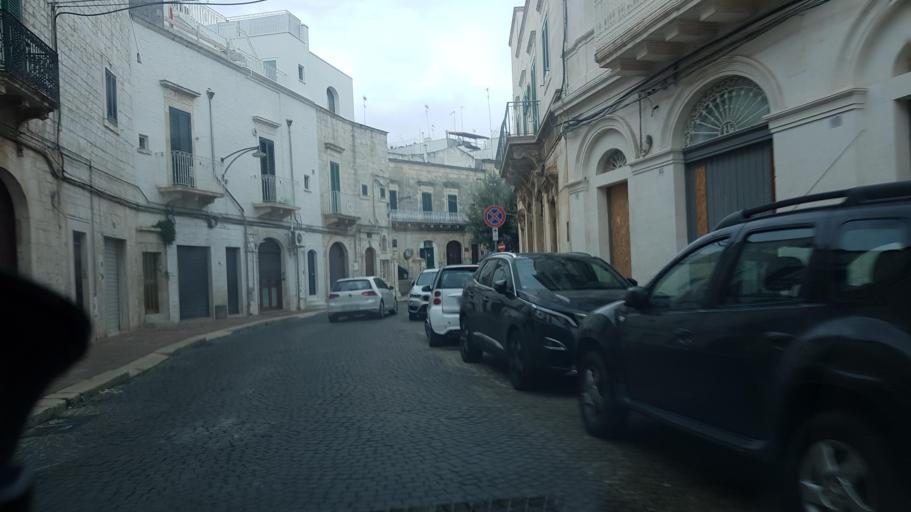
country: IT
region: Apulia
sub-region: Provincia di Brindisi
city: Ostuni
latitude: 40.7295
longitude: 17.5825
